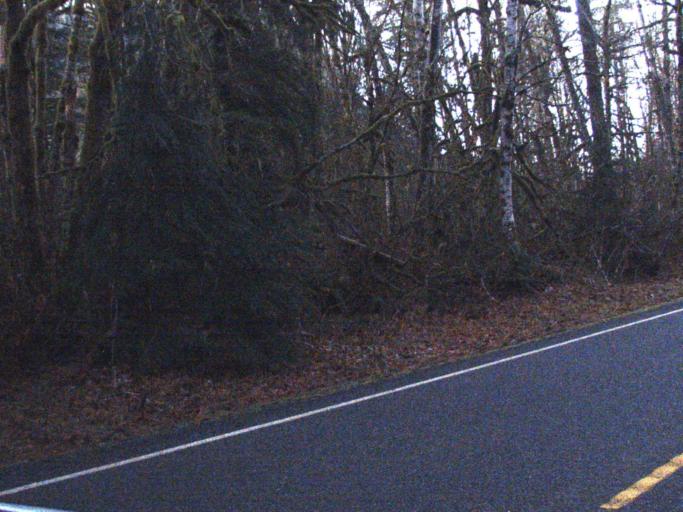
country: US
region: Washington
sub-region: Snohomish County
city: Darrington
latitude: 48.4318
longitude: -121.5700
